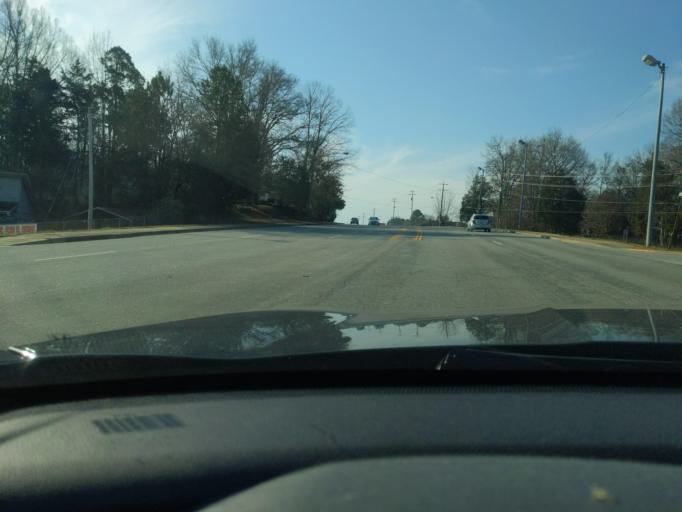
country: US
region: South Carolina
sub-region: Abbeville County
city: Abbeville
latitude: 34.1682
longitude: -82.3812
